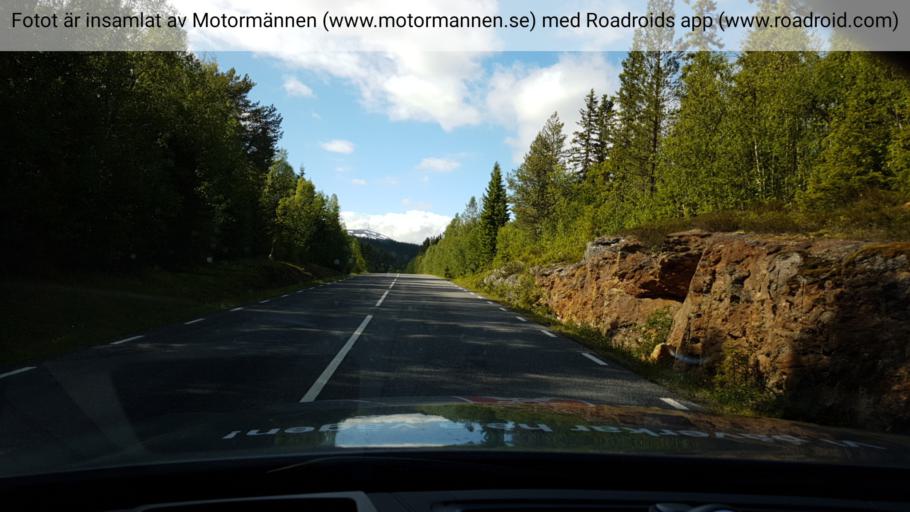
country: SE
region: Jaemtland
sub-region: Are Kommun
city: Are
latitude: 63.6978
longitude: 12.9679
